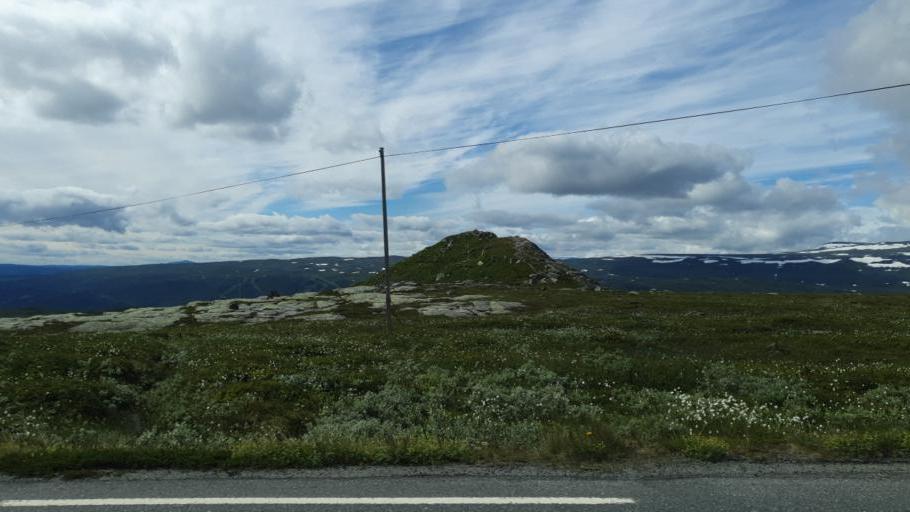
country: NO
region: Oppland
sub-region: Vestre Slidre
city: Slidre
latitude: 61.2827
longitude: 8.8339
